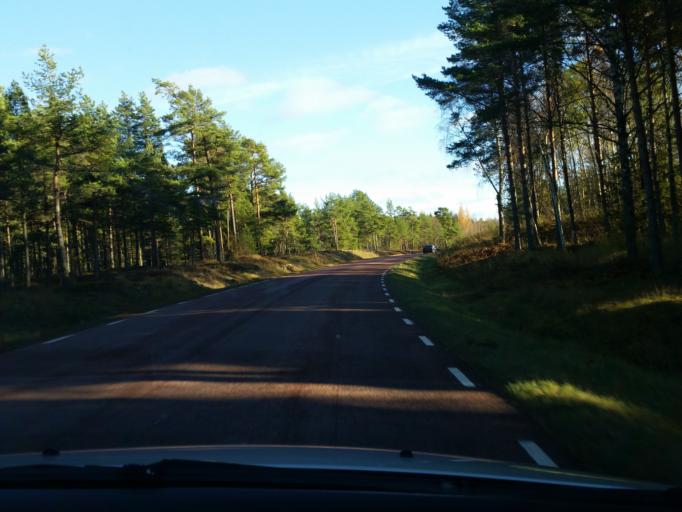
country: AX
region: Alands landsbygd
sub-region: Jomala
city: Jomala
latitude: 60.1593
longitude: 19.8948
